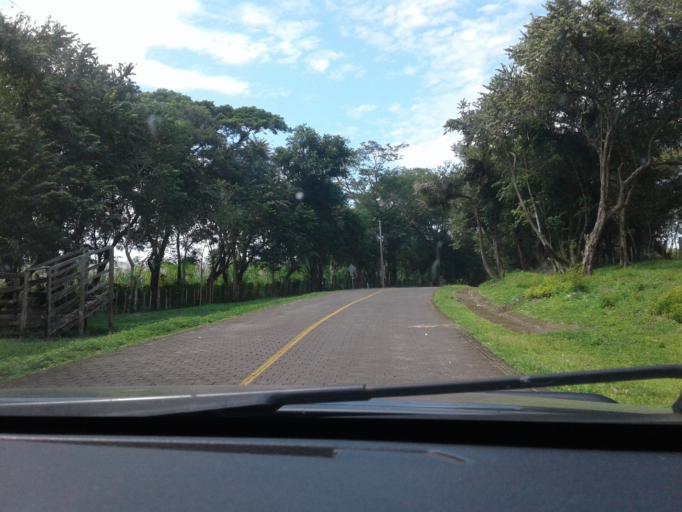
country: NI
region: Rivas
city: Cardenas
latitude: 11.1720
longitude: -85.4795
